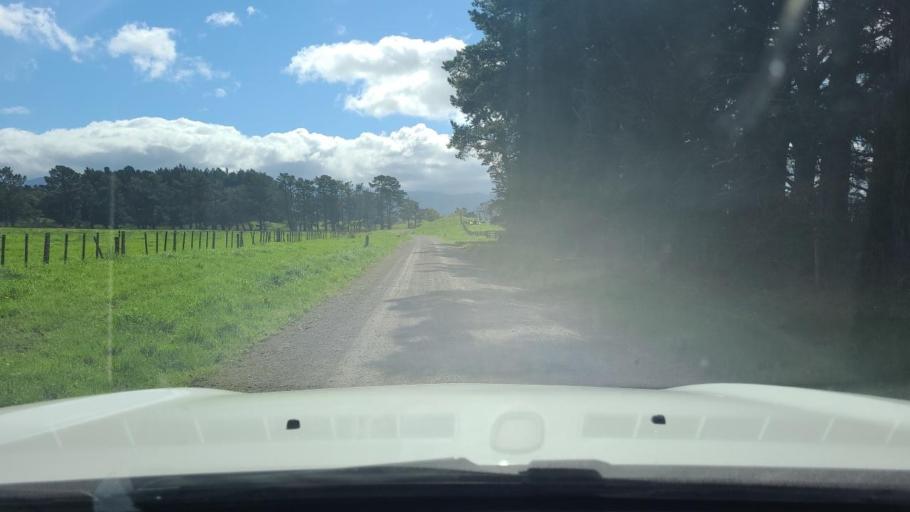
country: NZ
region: Wellington
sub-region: Upper Hutt City
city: Upper Hutt
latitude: -41.2374
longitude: 175.2973
